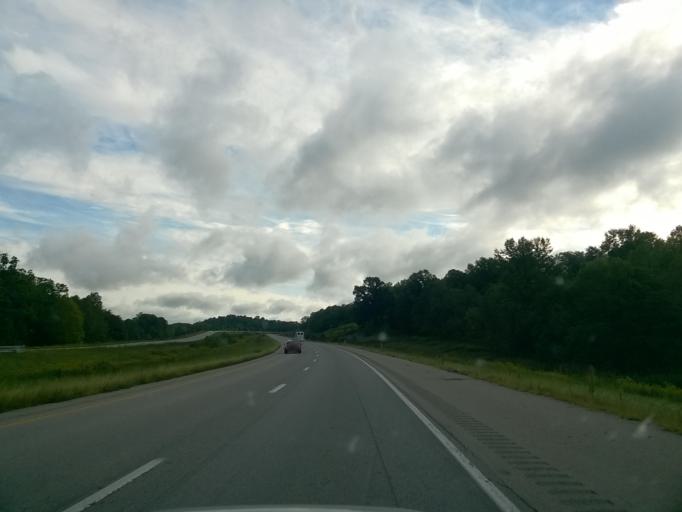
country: US
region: Indiana
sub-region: Crawford County
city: English
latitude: 38.2282
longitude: -86.6343
